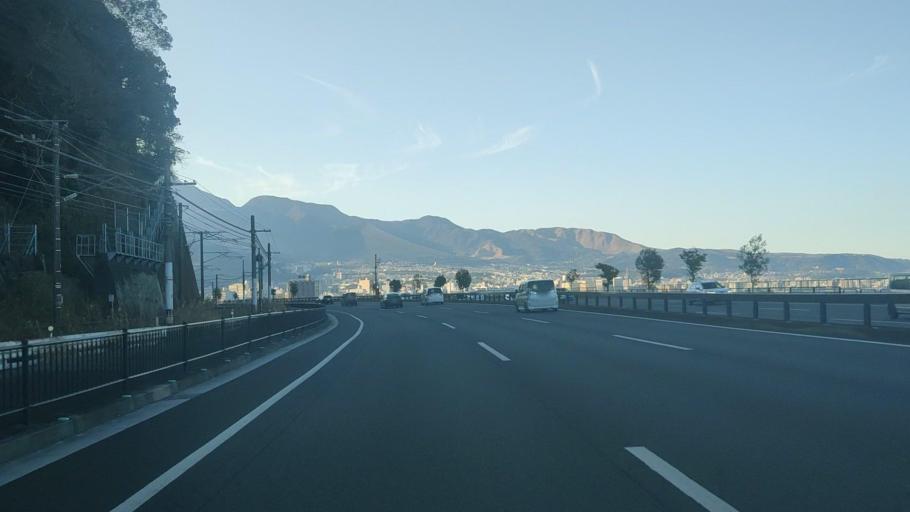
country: JP
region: Oita
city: Beppu
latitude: 33.2648
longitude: 131.5261
